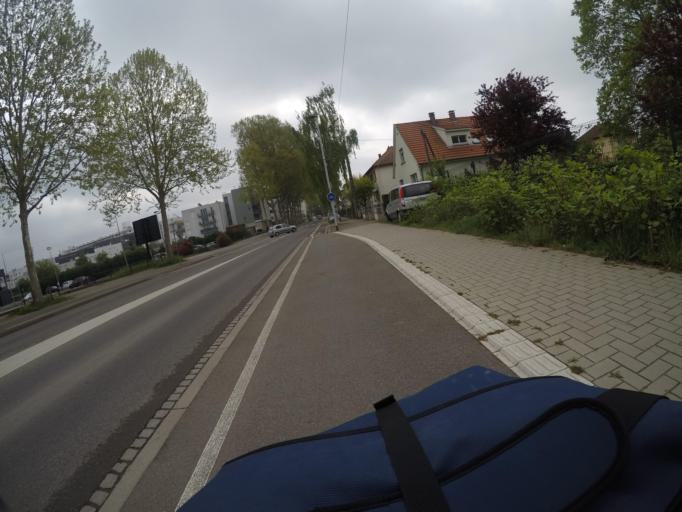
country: FR
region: Alsace
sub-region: Departement du Bas-Rhin
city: Oberhausbergen
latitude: 48.6033
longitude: 7.7068
